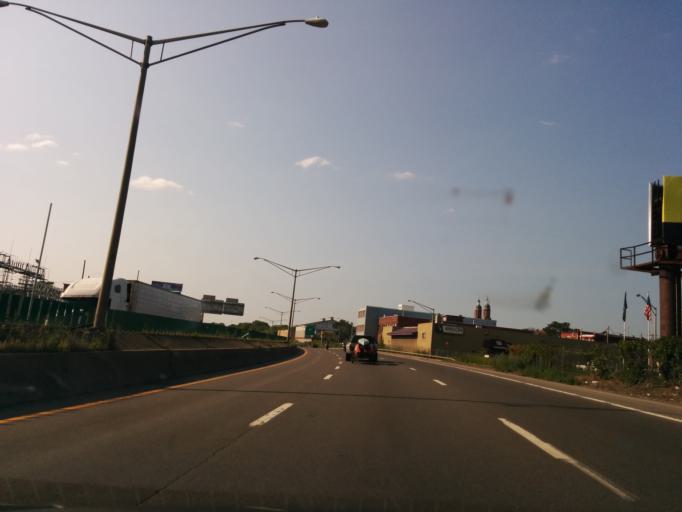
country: US
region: New York
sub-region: Onondaga County
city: Syracuse
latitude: 43.0576
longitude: -76.1539
